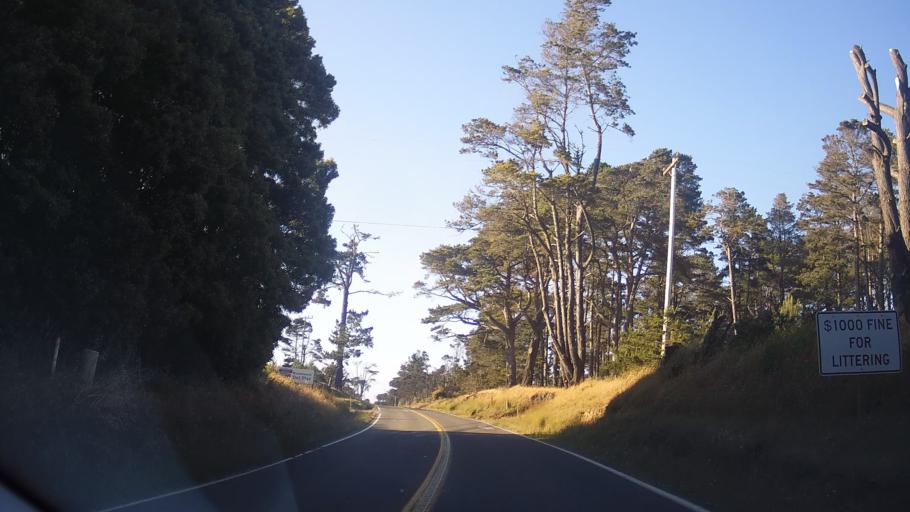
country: US
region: California
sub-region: Mendocino County
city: Fort Bragg
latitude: 39.4721
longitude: -123.7979
